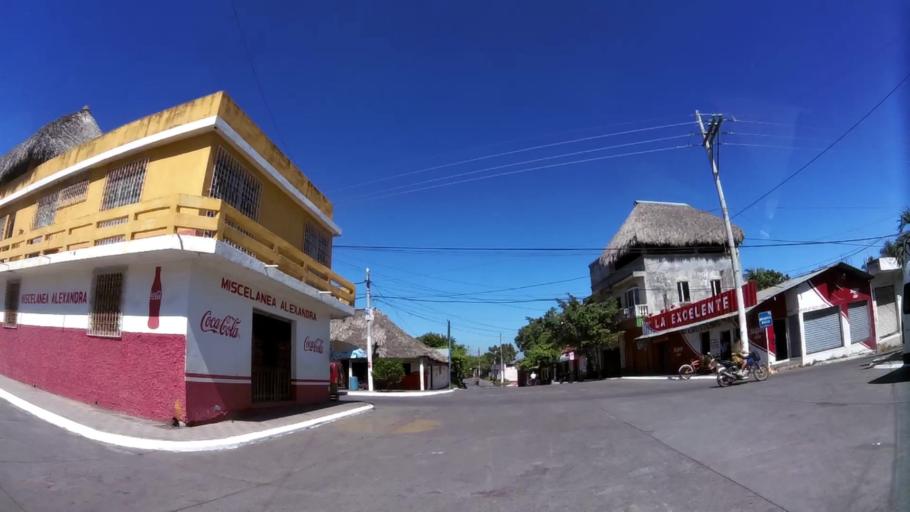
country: GT
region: Escuintla
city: Iztapa
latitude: 13.9305
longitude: -90.7132
